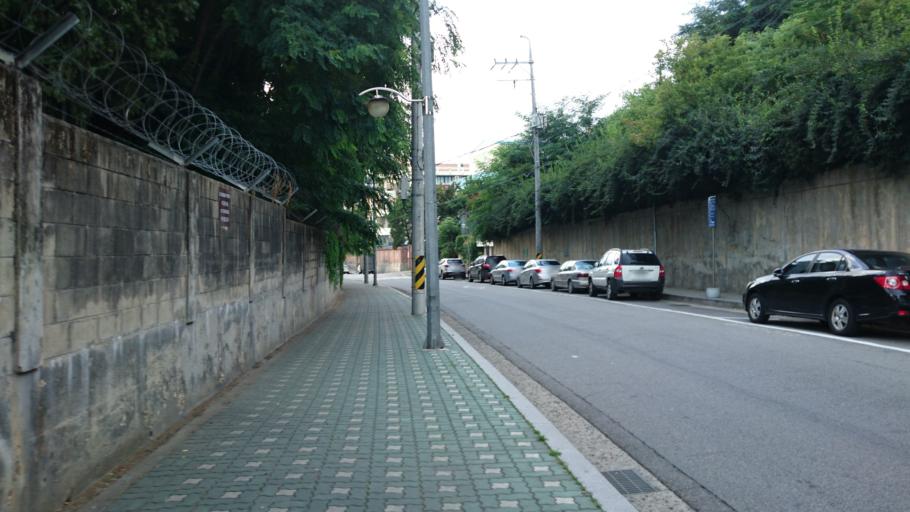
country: KR
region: Seoul
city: Seoul
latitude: 37.5439
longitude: 126.9791
